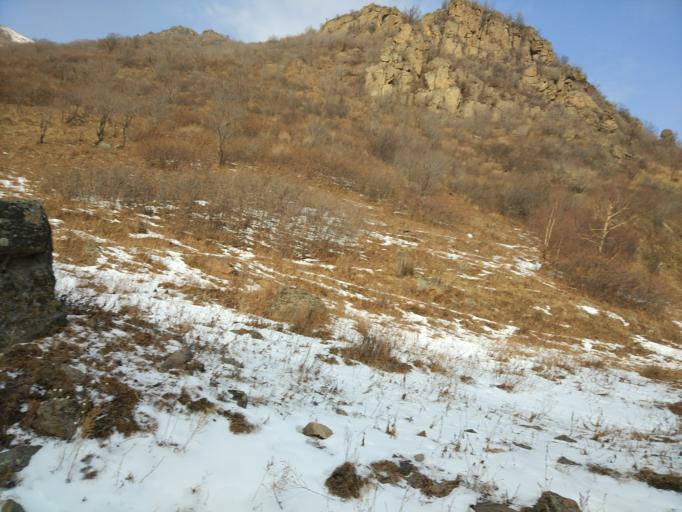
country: CN
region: Hebei
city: Xiwanzi
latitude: 40.8403
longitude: 115.4576
